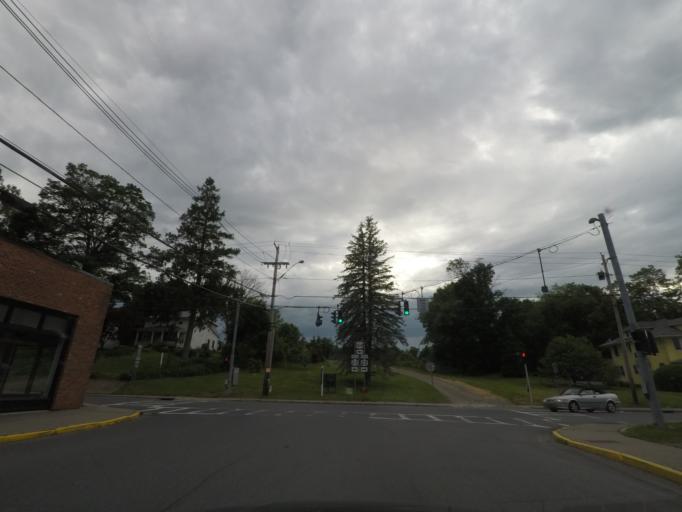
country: US
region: New York
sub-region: Dutchess County
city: Pine Plains
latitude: 41.9528
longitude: -73.5123
